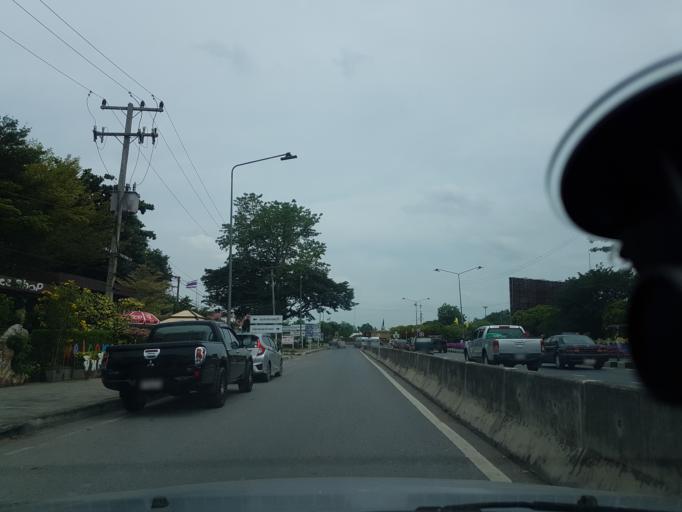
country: TH
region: Lop Buri
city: Lop Buri
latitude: 14.8014
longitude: 100.6527
